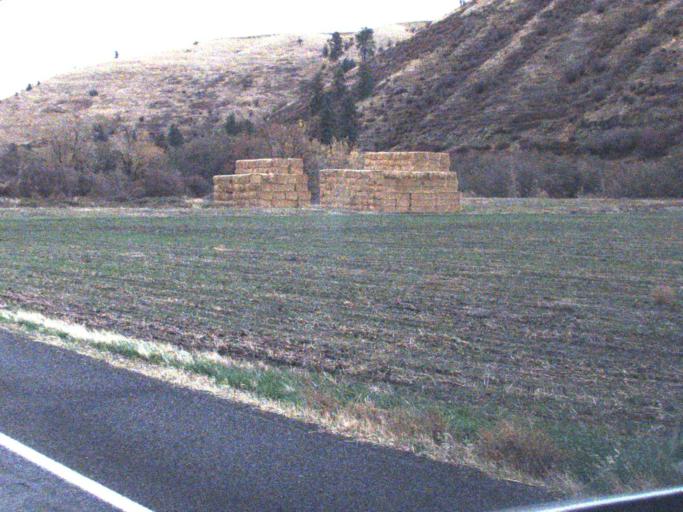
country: US
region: Washington
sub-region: Walla Walla County
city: Waitsburg
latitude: 46.2885
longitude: -118.0980
